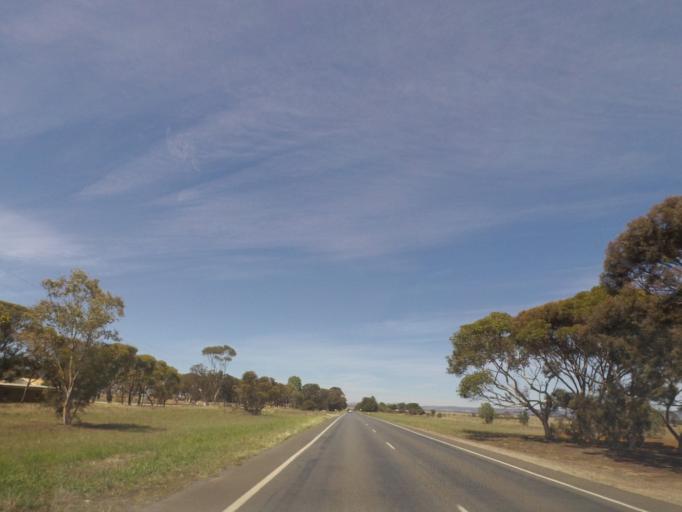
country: AU
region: Victoria
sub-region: Moorabool
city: Bacchus Marsh
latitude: -37.7915
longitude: 144.4181
